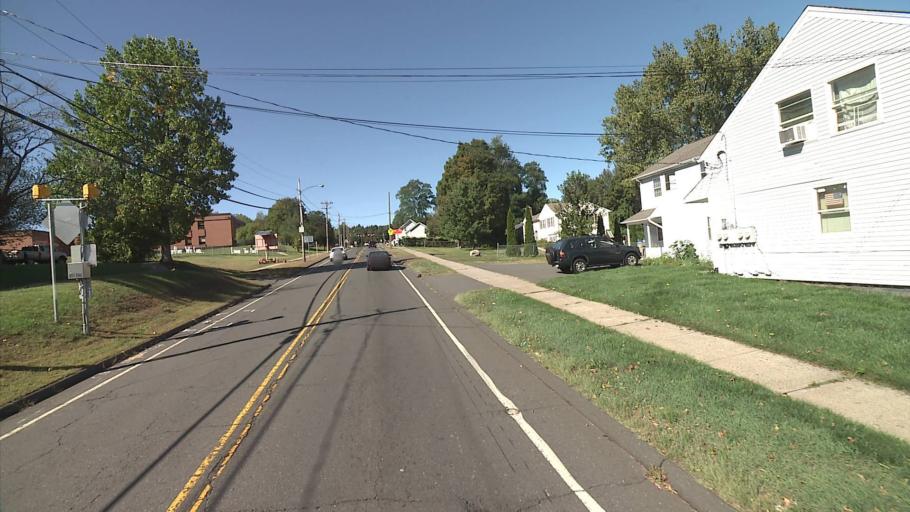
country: US
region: Connecticut
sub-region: Hartford County
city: Bristol
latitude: 41.6622
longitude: -72.9505
